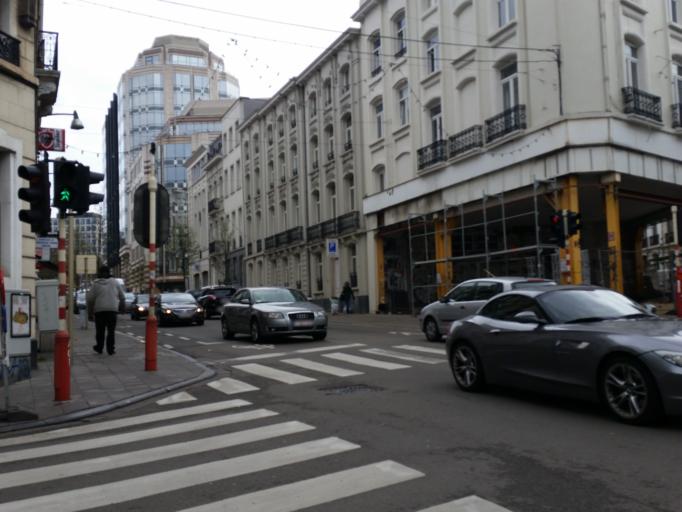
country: BE
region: Brussels Capital
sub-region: Bruxelles-Capitale
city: Brussels
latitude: 50.8324
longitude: 4.3497
